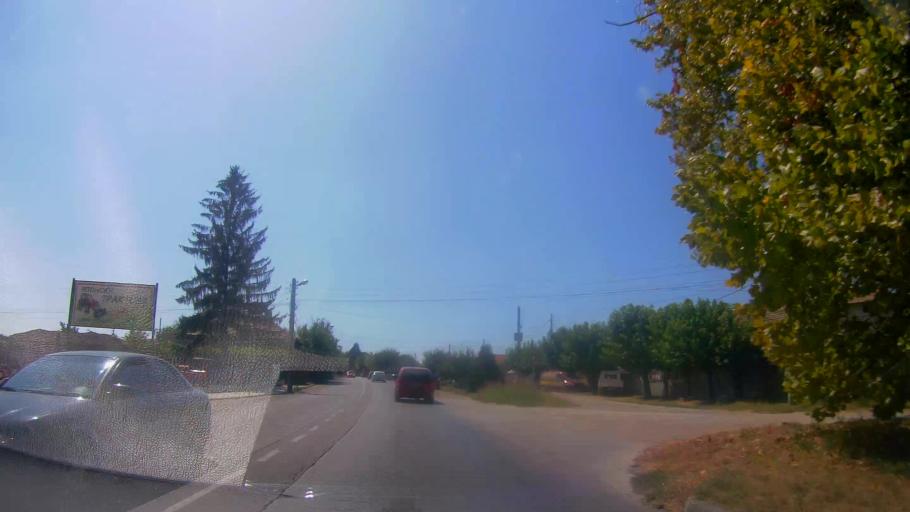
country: BG
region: Veliko Turnovo
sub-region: Obshtina Gorna Oryakhovitsa
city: Purvomaytsi
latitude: 43.1840
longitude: 25.6201
